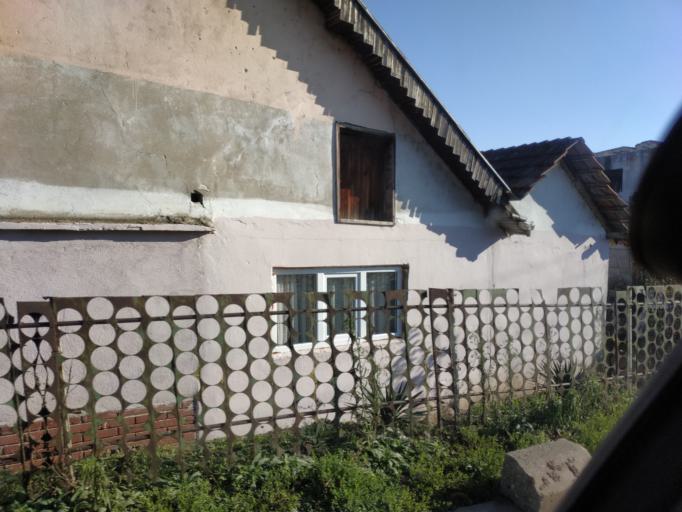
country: RS
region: Central Serbia
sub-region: Nisavski Okrug
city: Aleksinac
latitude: 43.5368
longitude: 21.7035
